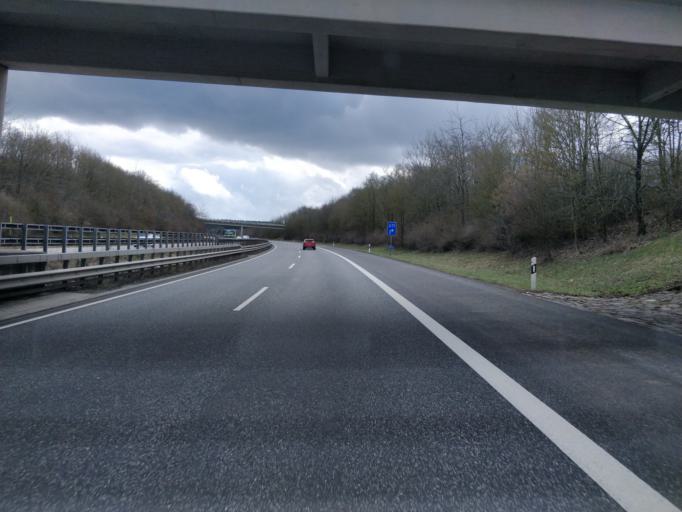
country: DE
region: Rheinland-Pfalz
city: Hasborn
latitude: 50.0526
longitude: 6.9044
